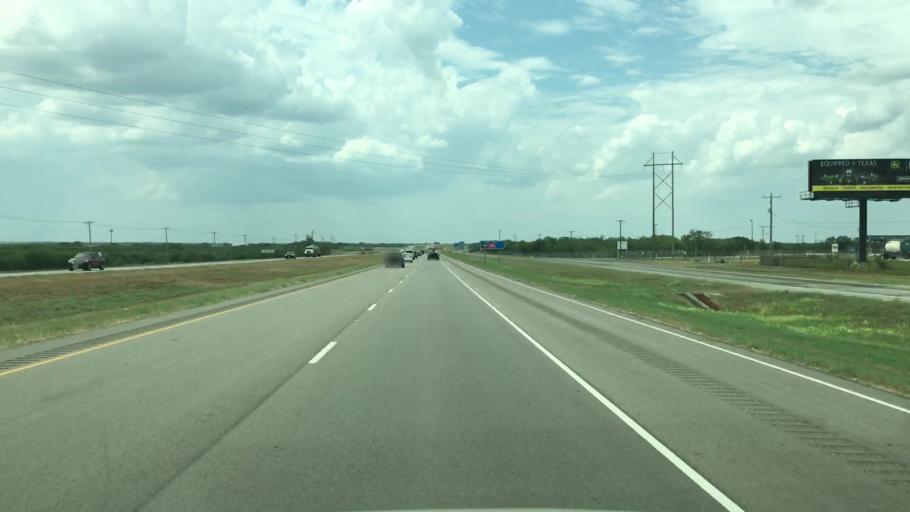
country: US
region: Texas
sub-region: Live Oak County
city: Three Rivers
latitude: 28.5130
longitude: -98.1712
